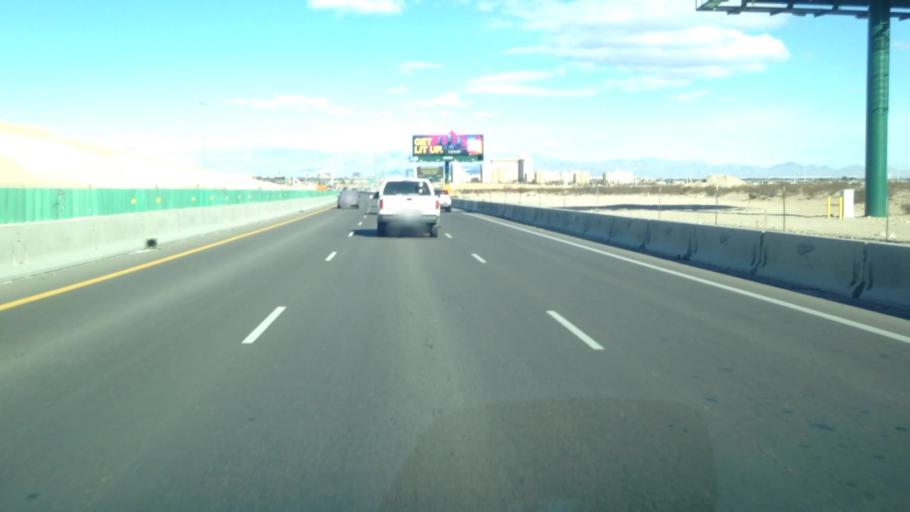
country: US
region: Nevada
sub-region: Clark County
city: Enterprise
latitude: 35.9858
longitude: -115.1803
